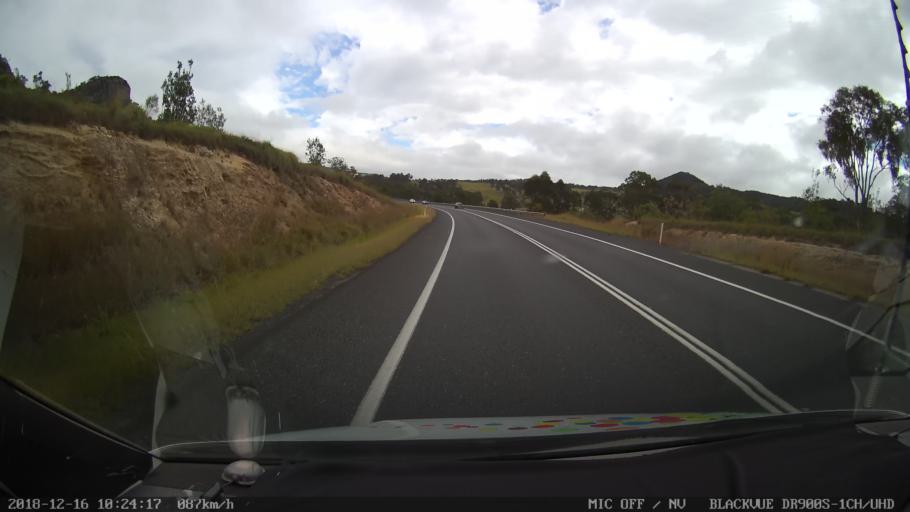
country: AU
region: New South Wales
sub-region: Tenterfield Municipality
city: Carrolls Creek
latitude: -29.1724
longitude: 152.0072
